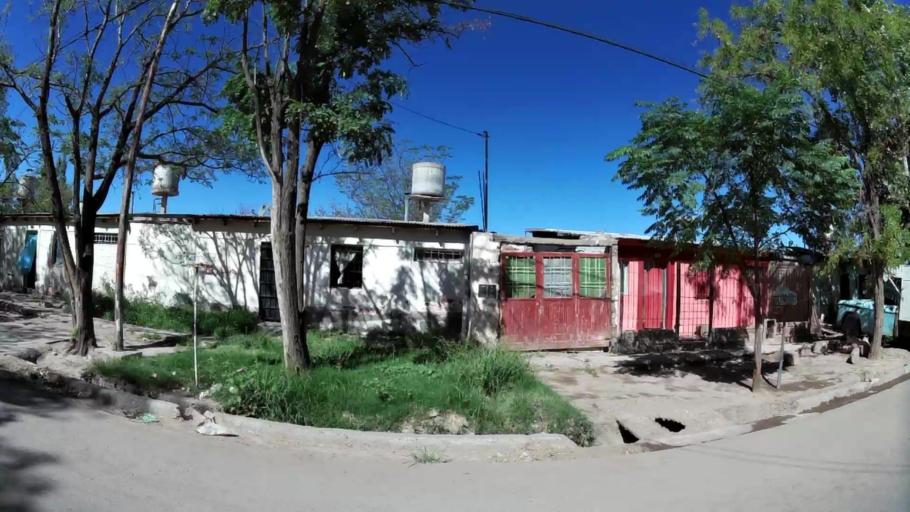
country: AR
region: Mendoza
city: Las Heras
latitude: -32.8249
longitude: -68.8154
